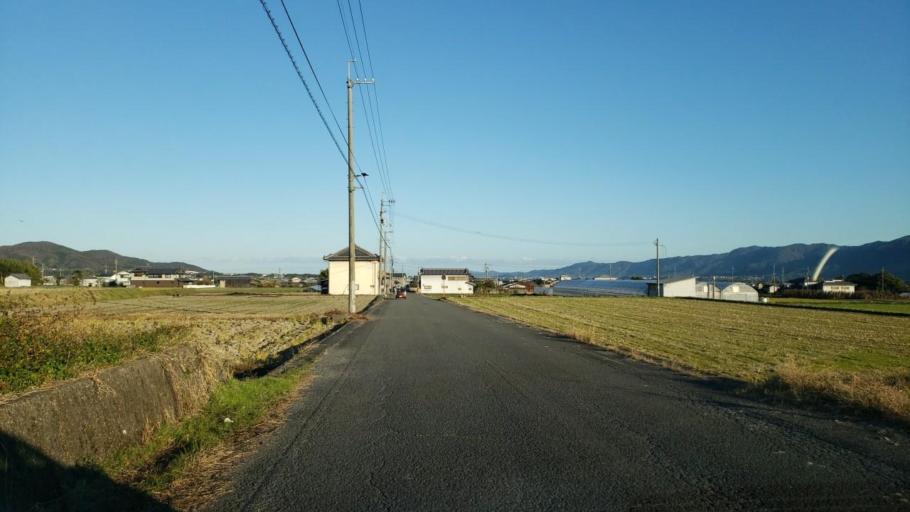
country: JP
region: Tokushima
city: Kamojimacho-jogejima
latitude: 34.0914
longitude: 134.2503
